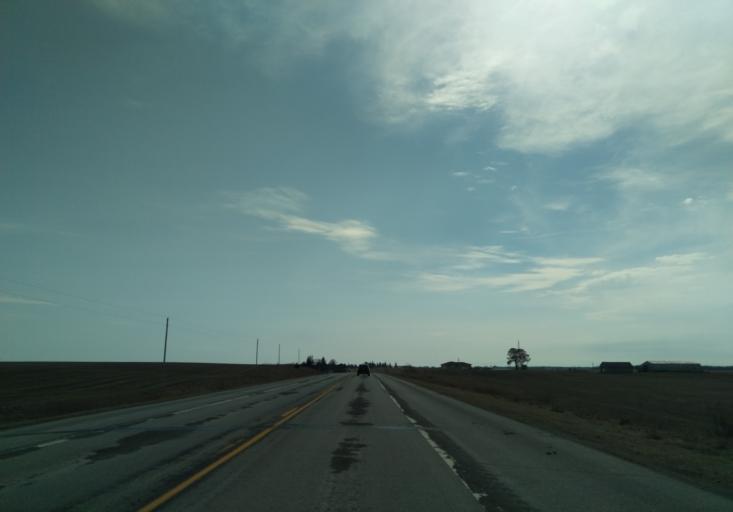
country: US
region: Minnesota
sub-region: Fillmore County
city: Harmony
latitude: 43.6042
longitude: -92.0098
